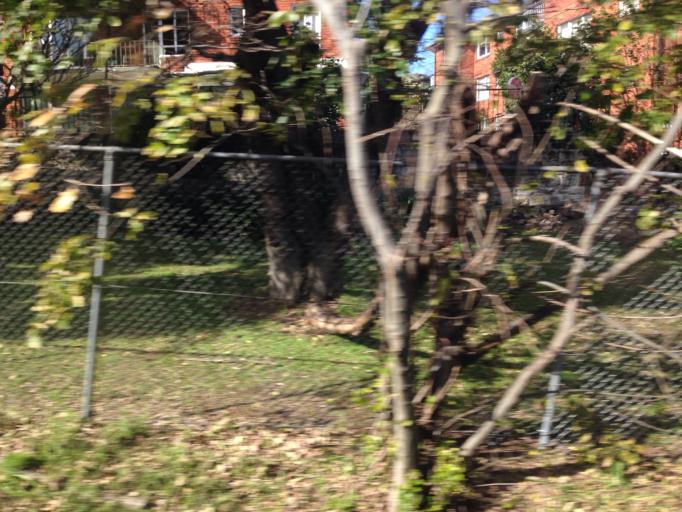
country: AU
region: New South Wales
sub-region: North Sydney
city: Wollstonecraft
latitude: -33.8305
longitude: 151.1922
